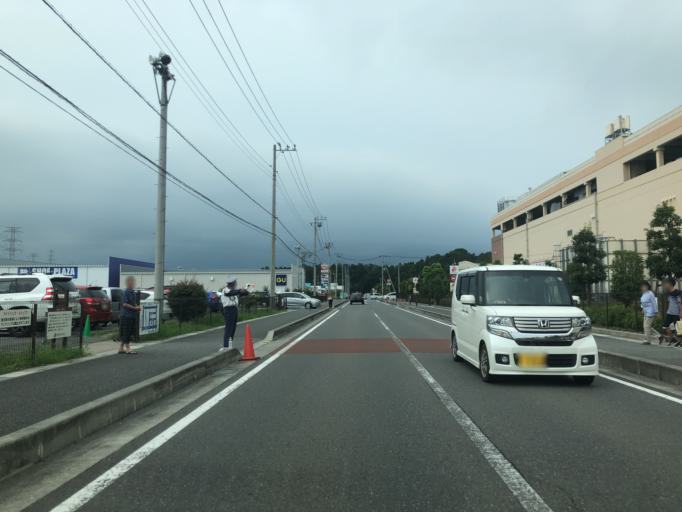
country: JP
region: Saitama
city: Sakado
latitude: 36.0058
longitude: 139.4117
